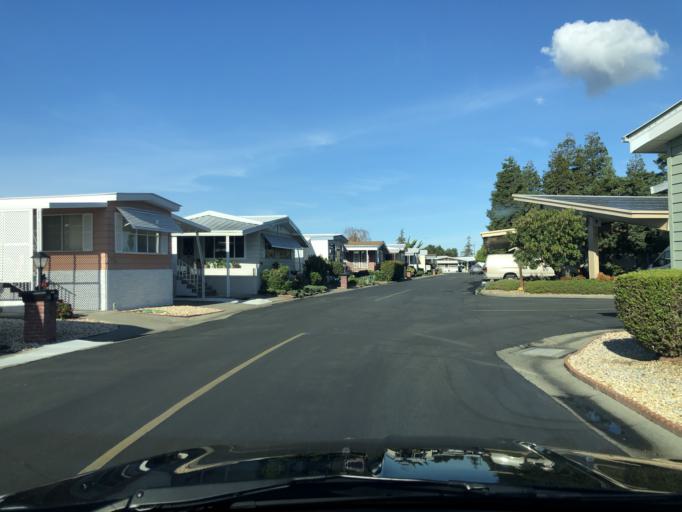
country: US
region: California
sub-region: Contra Costa County
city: Pacheco
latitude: 37.9936
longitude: -122.0651
